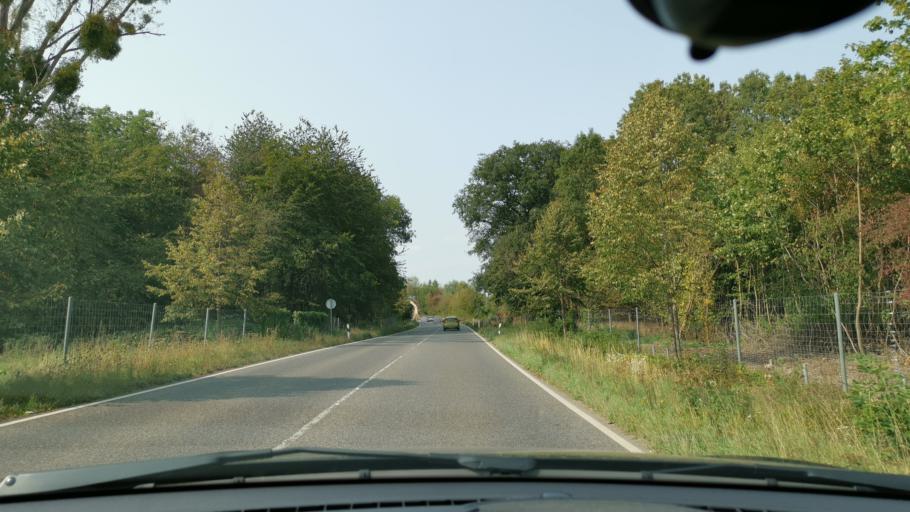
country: DE
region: North Rhine-Westphalia
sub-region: Regierungsbezirk Koln
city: Bergheim
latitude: 50.9703
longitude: 6.6121
